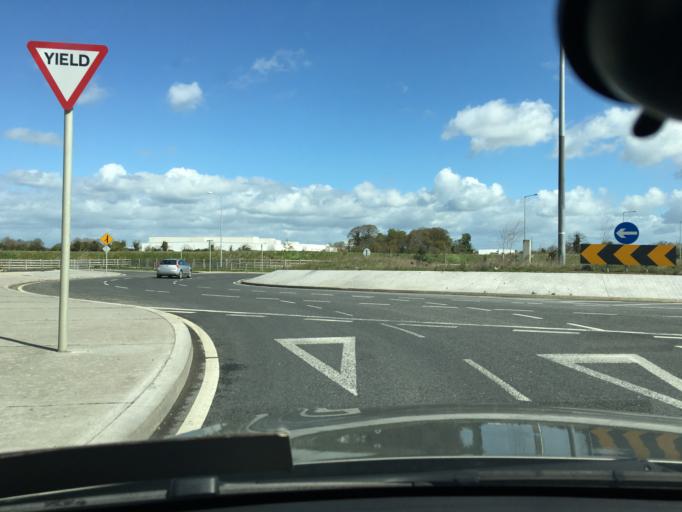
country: IE
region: Leinster
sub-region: Fingal County
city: Blanchardstown
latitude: 53.4264
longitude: -6.3591
